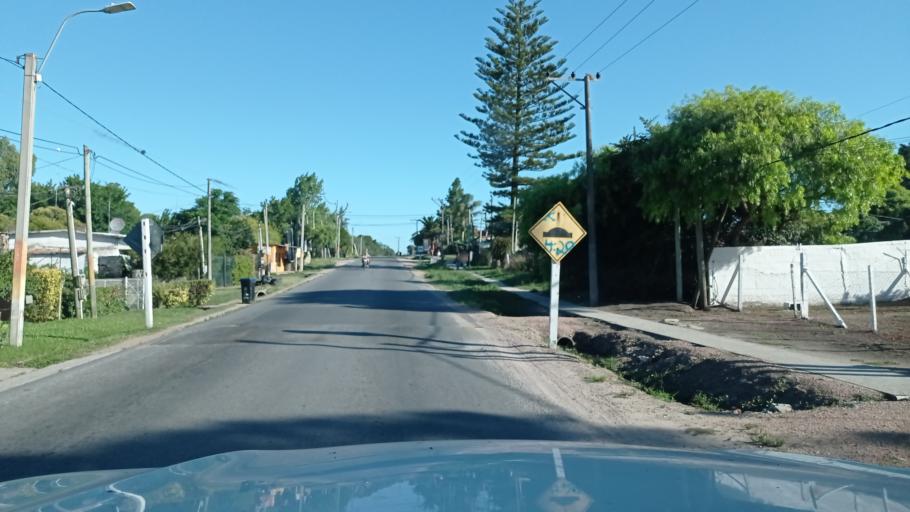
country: UY
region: Canelones
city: Colonia Nicolich
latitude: -34.8215
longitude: -56.0040
